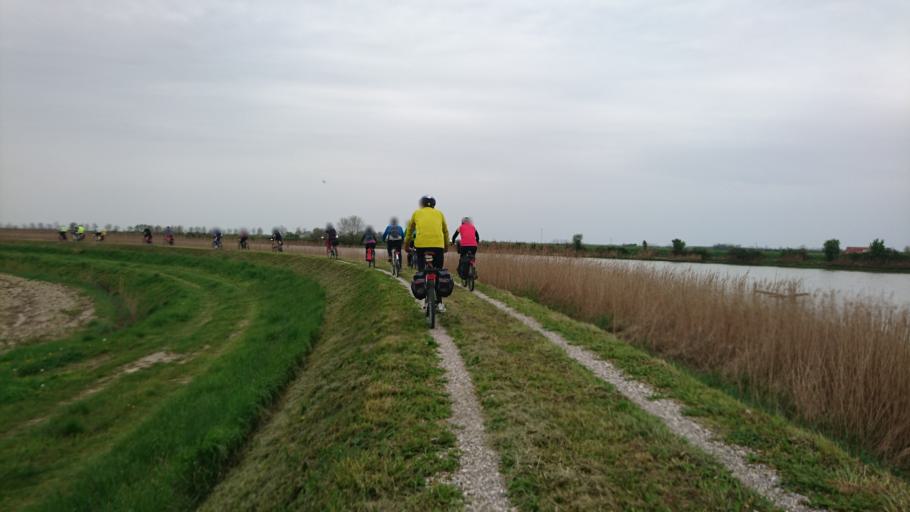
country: IT
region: Veneto
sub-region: Provincia di Venezia
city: Lugugnana
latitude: 45.6752
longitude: 12.9562
